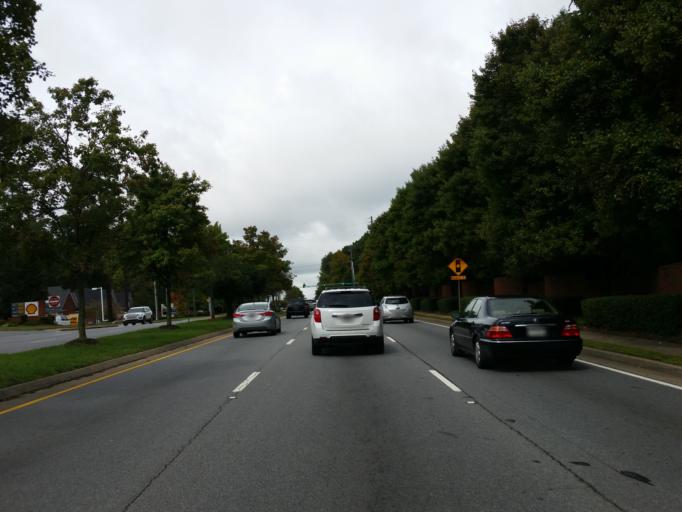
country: US
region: Georgia
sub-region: Fulton County
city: Sandy Springs
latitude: 33.9506
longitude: -84.4113
